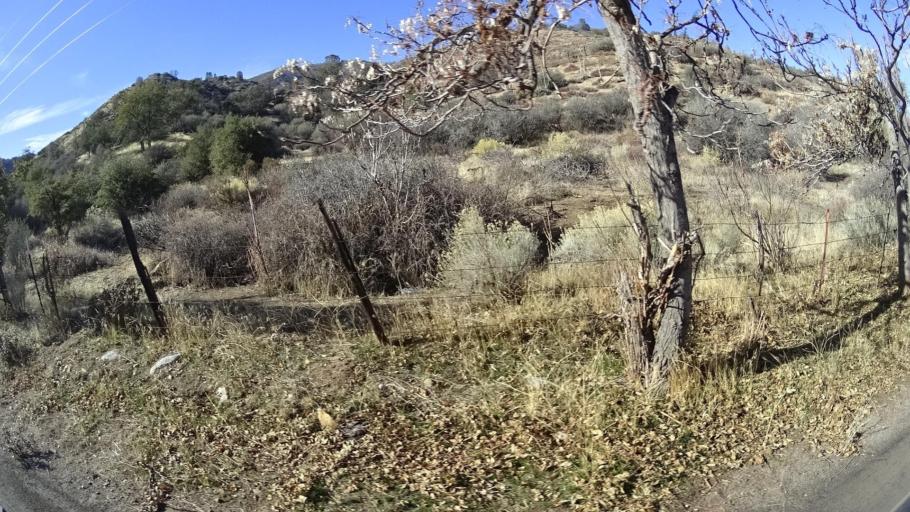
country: US
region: California
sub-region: Kern County
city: Bodfish
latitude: 35.5104
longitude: -118.5198
